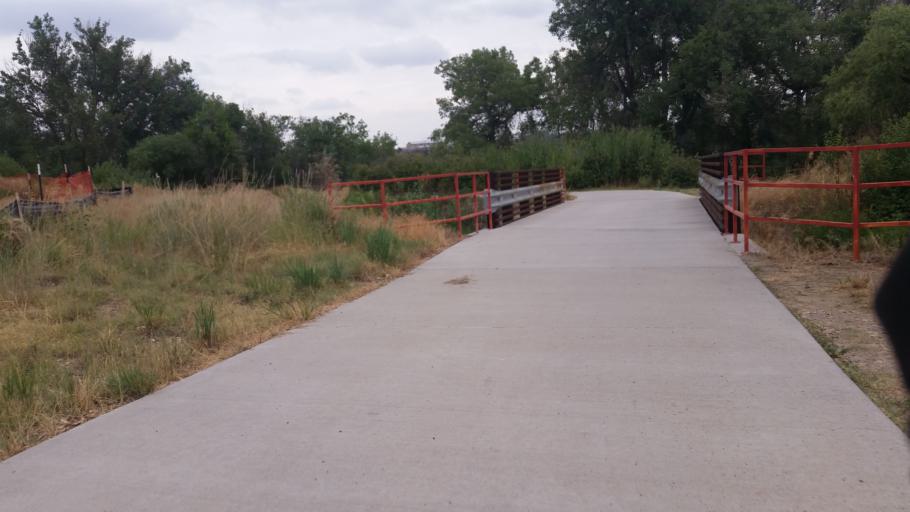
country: US
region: Colorado
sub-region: Adams County
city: Twin Lakes
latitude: 39.8164
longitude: -105.0014
